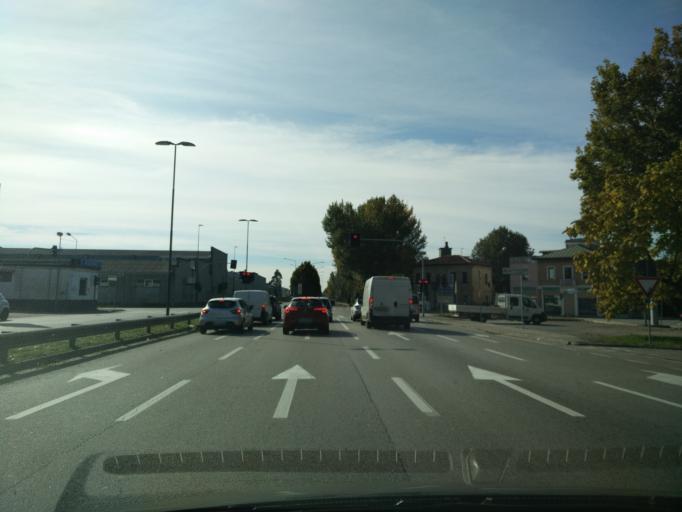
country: IT
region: Veneto
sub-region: Provincia di Venezia
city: Mestre
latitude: 45.4771
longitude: 12.2323
